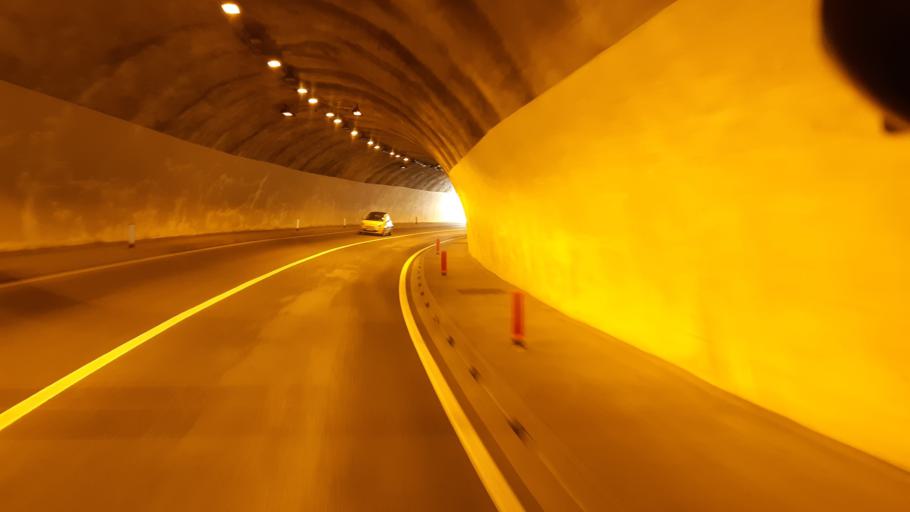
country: SI
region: Trzic
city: Trzic
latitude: 46.3630
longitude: 14.3052
